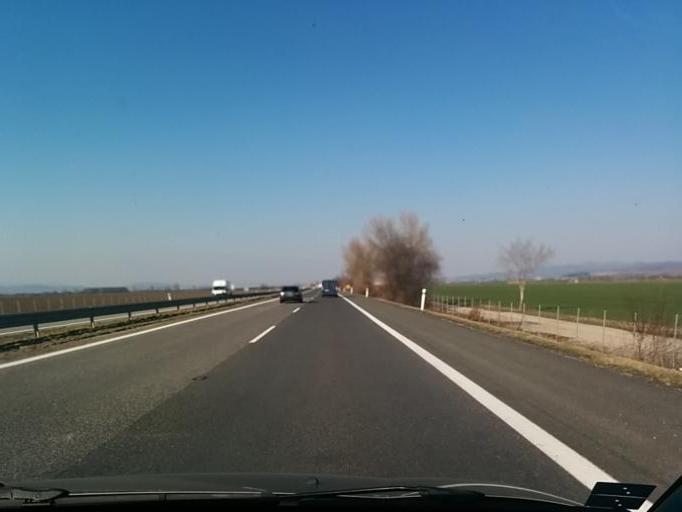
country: SK
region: Trnavsky
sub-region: Okres Trnava
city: Piestany
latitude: 48.5324
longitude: 17.7826
